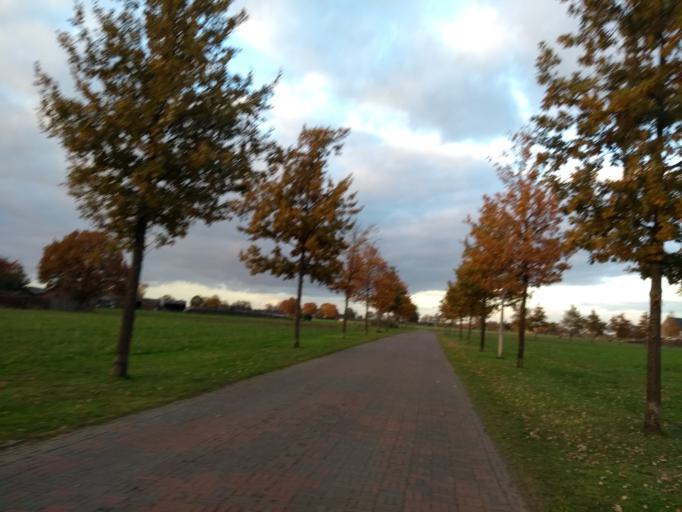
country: NL
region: Overijssel
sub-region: Gemeente Almelo
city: Almelo
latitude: 52.3829
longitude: 6.6962
